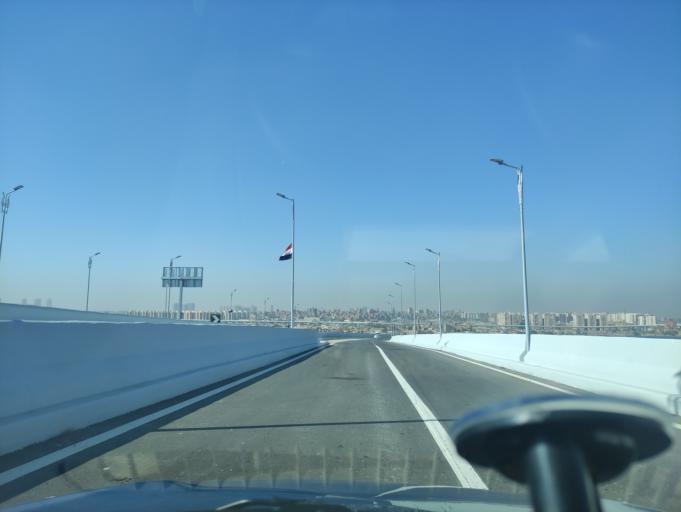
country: EG
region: Al Jizah
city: Al Jizah
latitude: 30.0074
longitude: 31.2679
